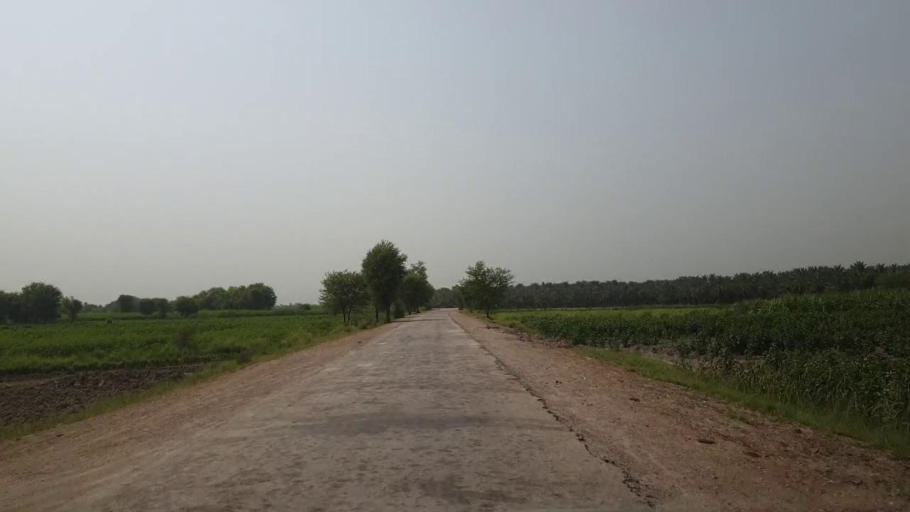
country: PK
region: Sindh
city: Gambat
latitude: 27.4319
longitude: 68.5338
